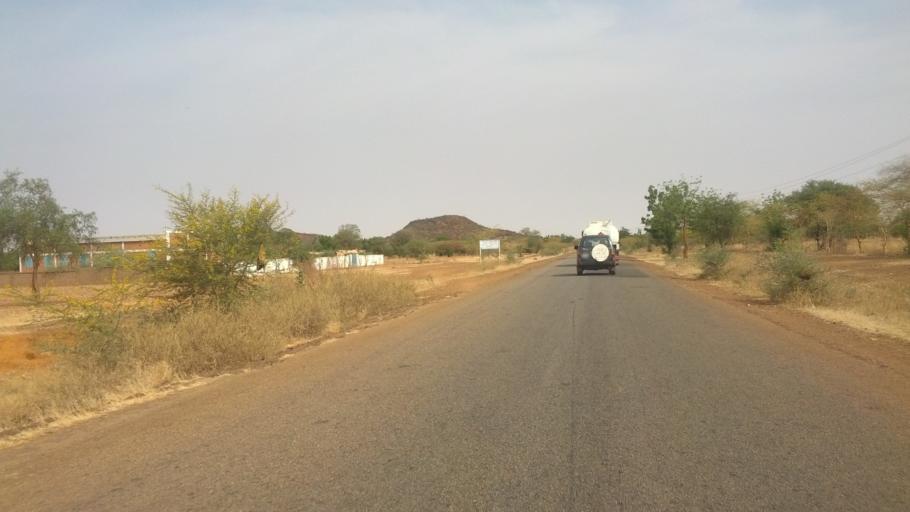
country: BF
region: Centre-Nord
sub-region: Province du Sanmatenga
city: Kaya
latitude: 12.9182
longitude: -1.0778
